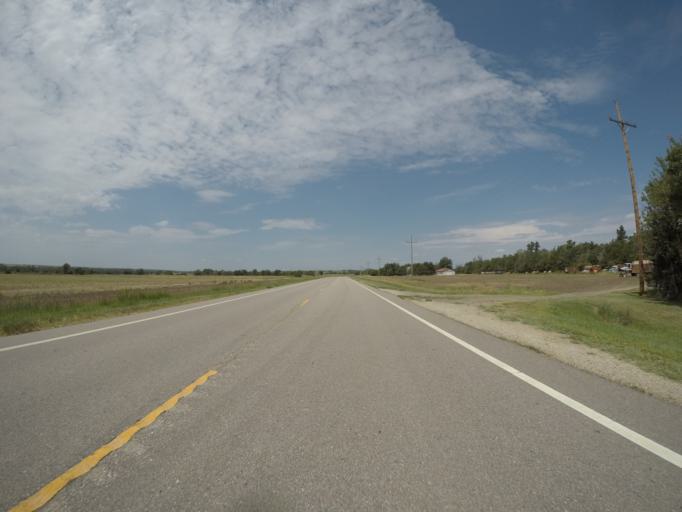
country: US
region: Kansas
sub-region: Rooks County
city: Stockton
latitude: 39.4448
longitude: -99.2285
